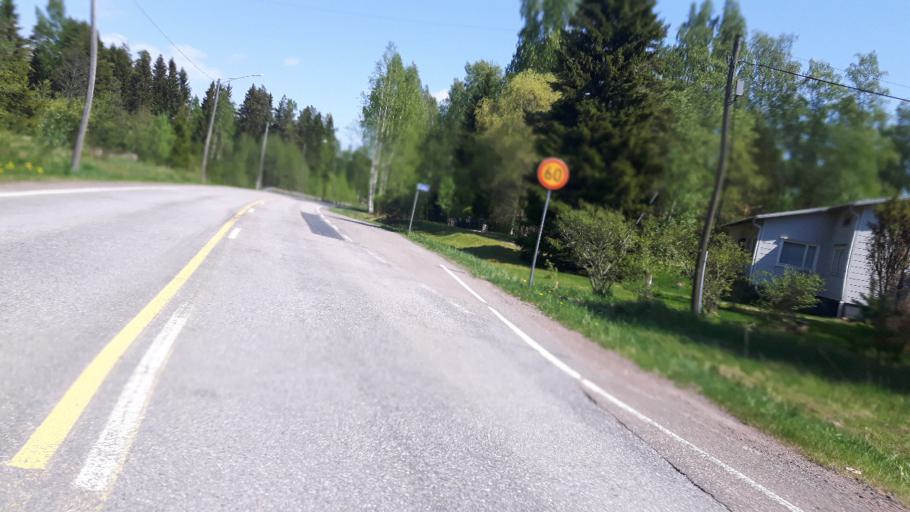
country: FI
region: Uusimaa
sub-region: Loviisa
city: Ruotsinpyhtaeae
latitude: 60.4982
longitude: 26.4436
